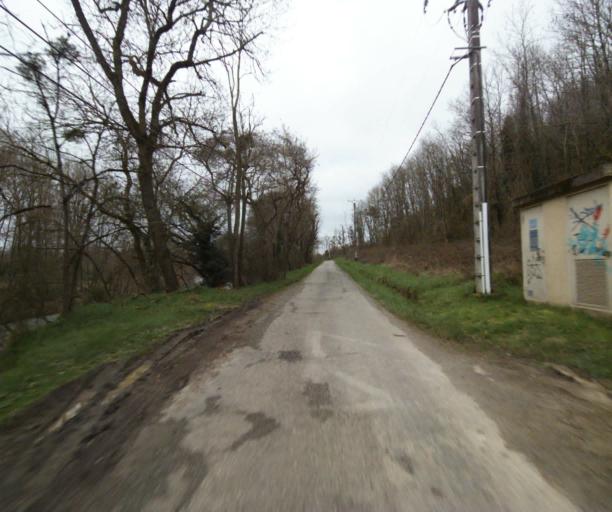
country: FR
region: Midi-Pyrenees
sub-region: Departement de l'Ariege
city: Saverdun
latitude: 43.2230
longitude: 1.5860
